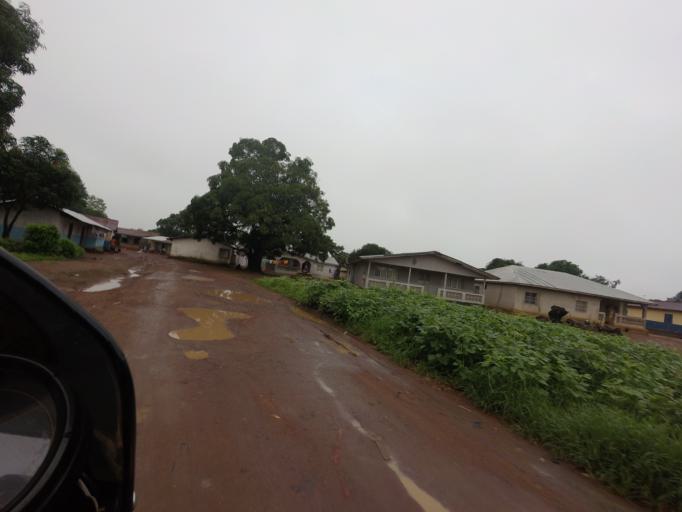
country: SL
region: Northern Province
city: Kambia
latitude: 9.1094
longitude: -12.9272
